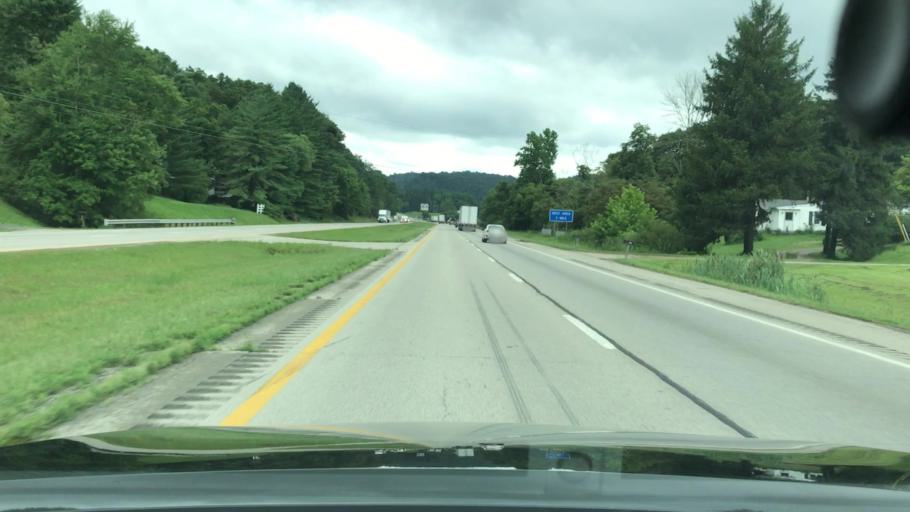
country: US
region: Ohio
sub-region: Jackson County
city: Jackson
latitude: 39.1780
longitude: -82.7491
